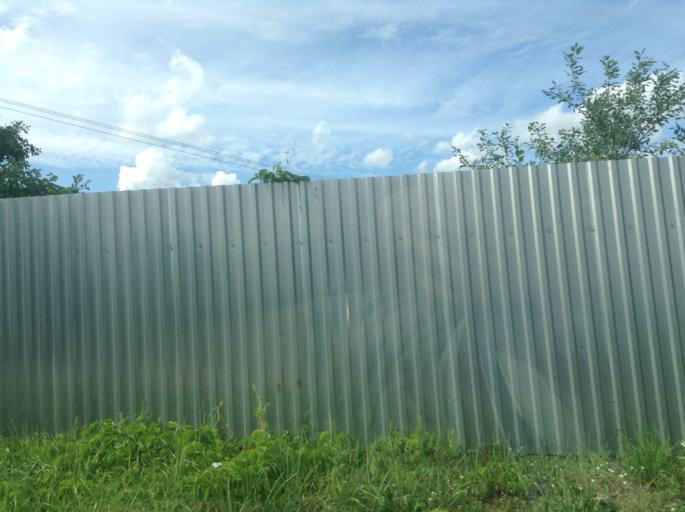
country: RU
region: Moskovskaya
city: Yegor'yevsk
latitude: 55.3654
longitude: 39.0966
